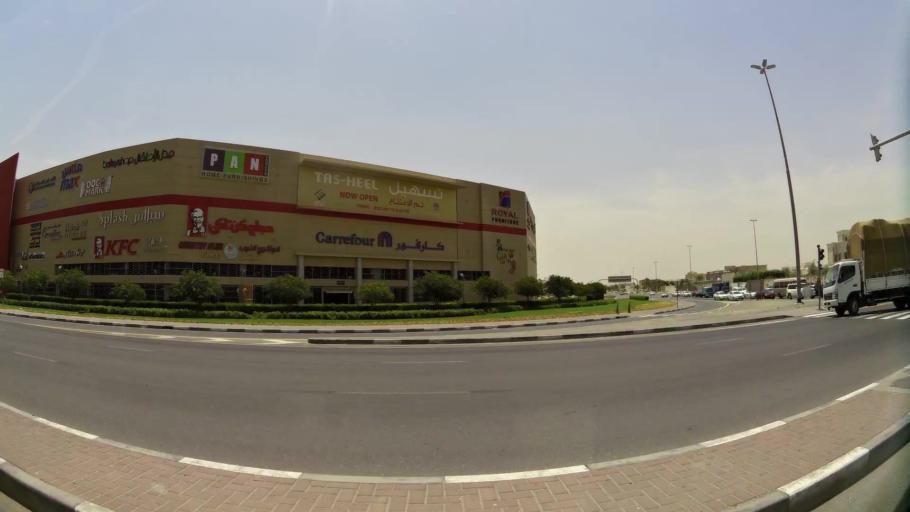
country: AE
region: Ash Shariqah
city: Sharjah
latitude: 25.2811
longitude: 55.3968
